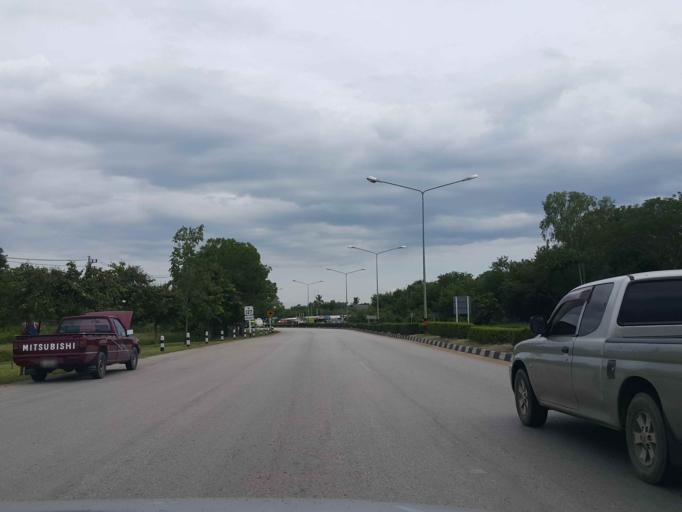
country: TH
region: Lampang
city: Lampang
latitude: 18.2638
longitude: 99.4680
